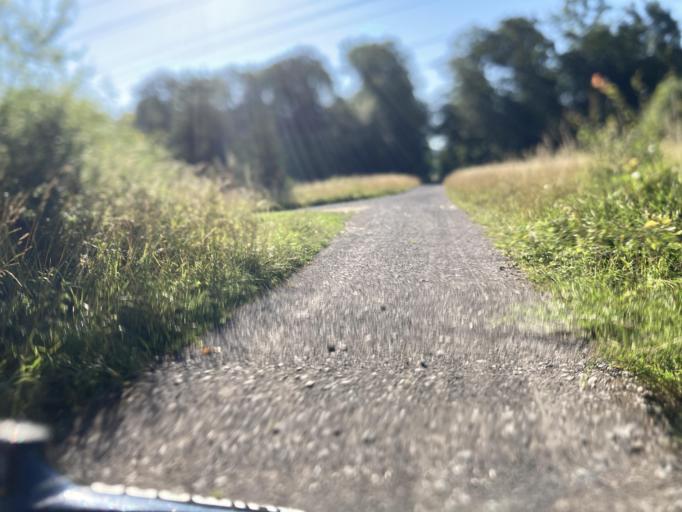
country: DE
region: Baden-Wuerttemberg
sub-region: Regierungsbezirk Stuttgart
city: Renningen
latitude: 48.7828
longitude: 8.9710
